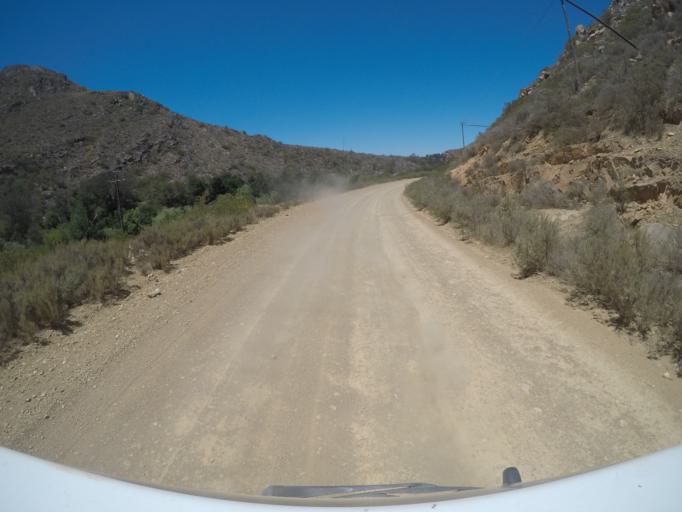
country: ZA
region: Western Cape
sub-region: Overberg District Municipality
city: Caledon
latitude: -34.1179
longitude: 19.2352
